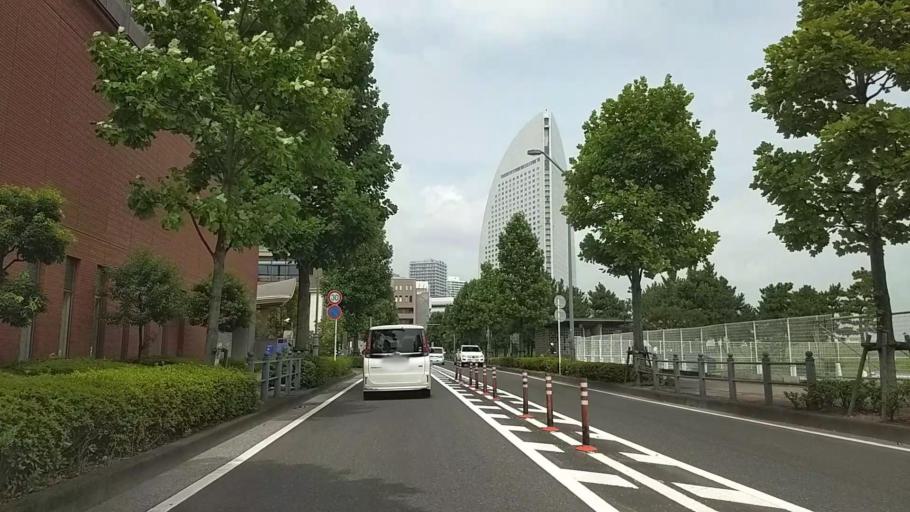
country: JP
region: Kanagawa
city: Yokohama
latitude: 35.4549
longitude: 139.6409
